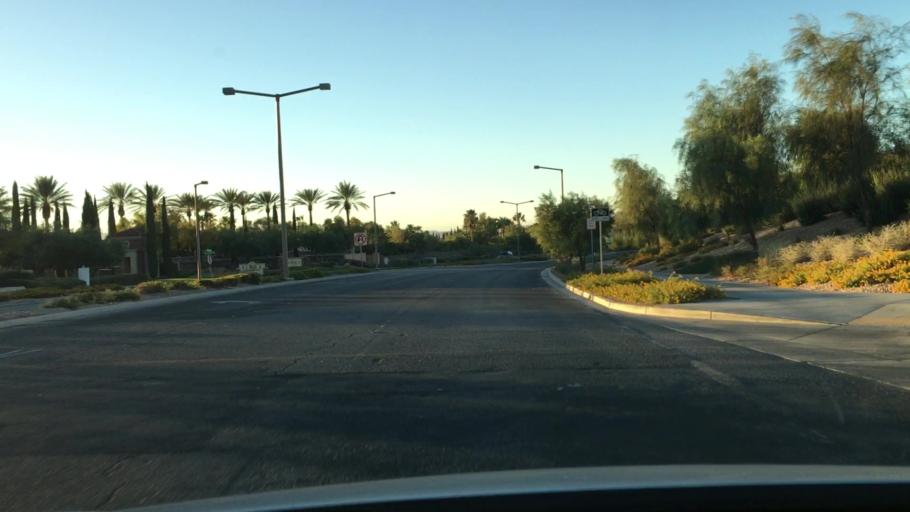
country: US
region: Nevada
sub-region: Clark County
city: Summerlin South
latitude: 36.1086
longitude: -115.3282
